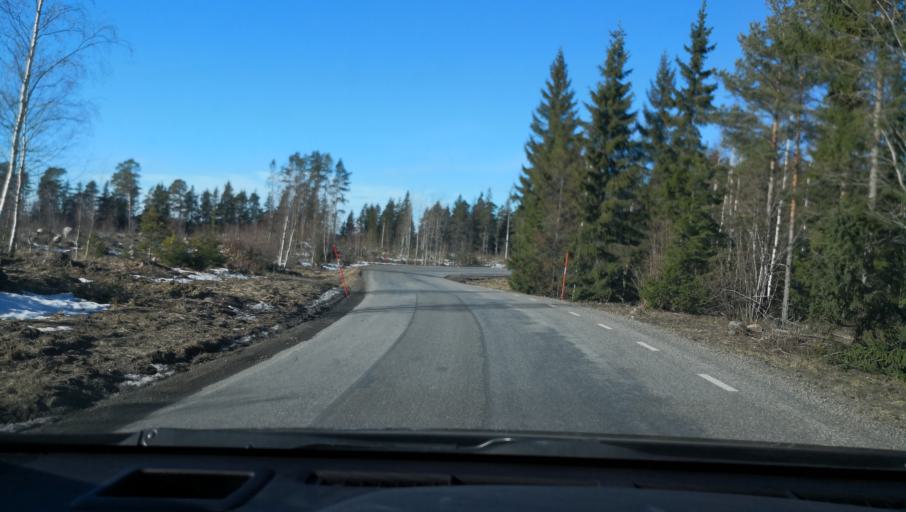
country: SE
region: Uppsala
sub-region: Osthammars Kommun
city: Osterbybruk
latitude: 60.2302
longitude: 17.9190
